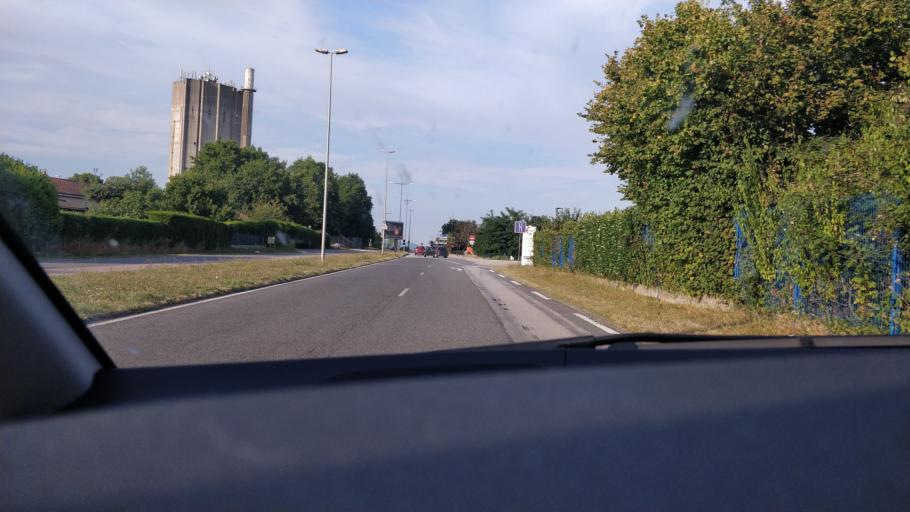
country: FR
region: Limousin
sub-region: Departement de la Haute-Vienne
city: Le Palais-sur-Vienne
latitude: 45.8696
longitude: 1.2977
